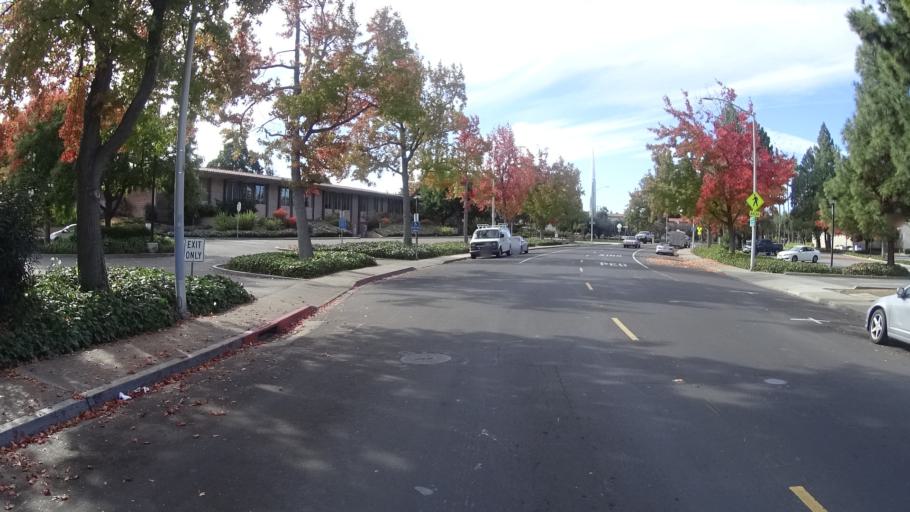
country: US
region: California
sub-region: Santa Clara County
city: Santa Clara
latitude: 37.3555
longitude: -121.9536
